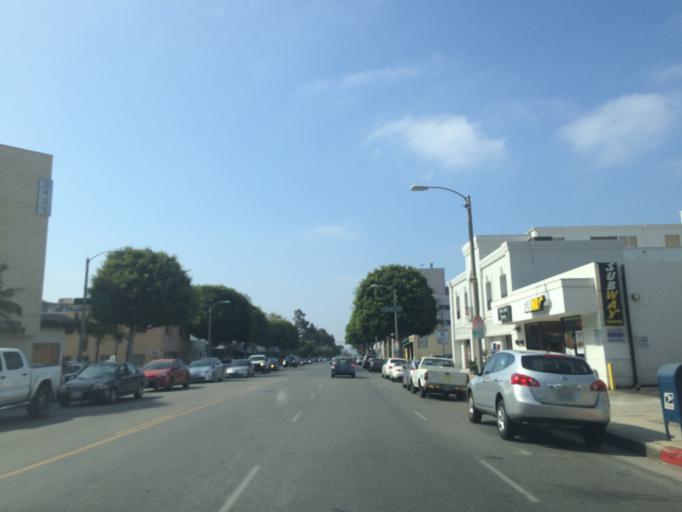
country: US
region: California
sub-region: Los Angeles County
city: Beverly Hills
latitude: 34.0644
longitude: -118.3763
